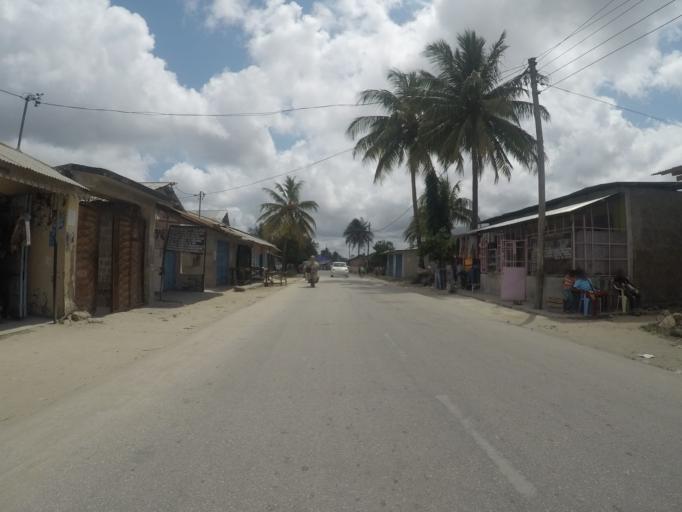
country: TZ
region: Zanzibar Urban/West
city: Zanzibar
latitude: -6.1944
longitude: 39.2444
